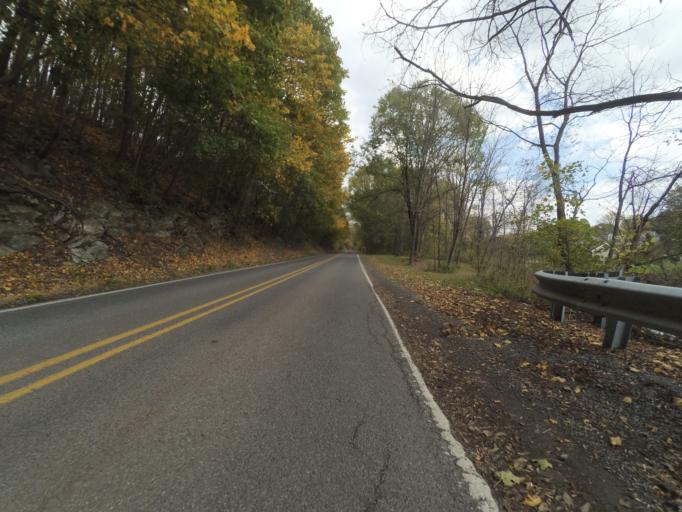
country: US
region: Pennsylvania
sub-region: Centre County
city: Bellefonte
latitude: 40.9058
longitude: -77.7940
